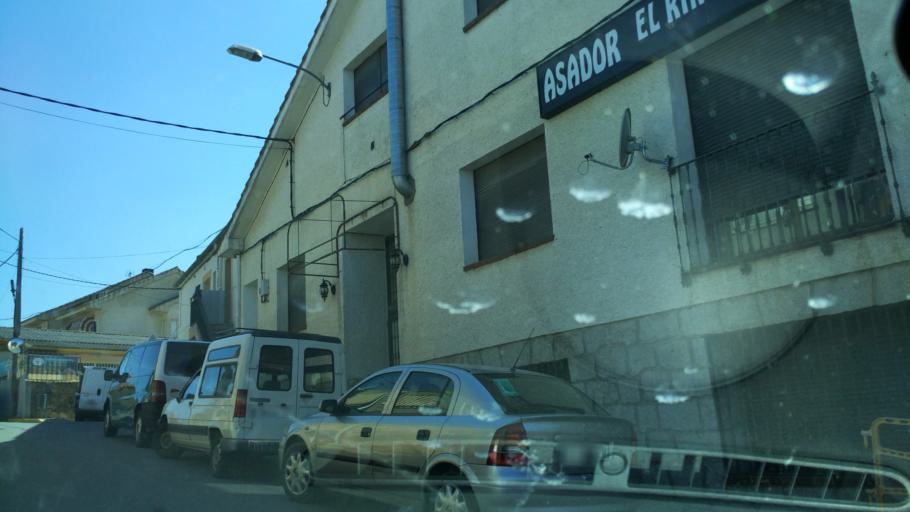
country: ES
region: Madrid
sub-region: Provincia de Madrid
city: Pedrezuela
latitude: 40.7439
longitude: -3.6005
